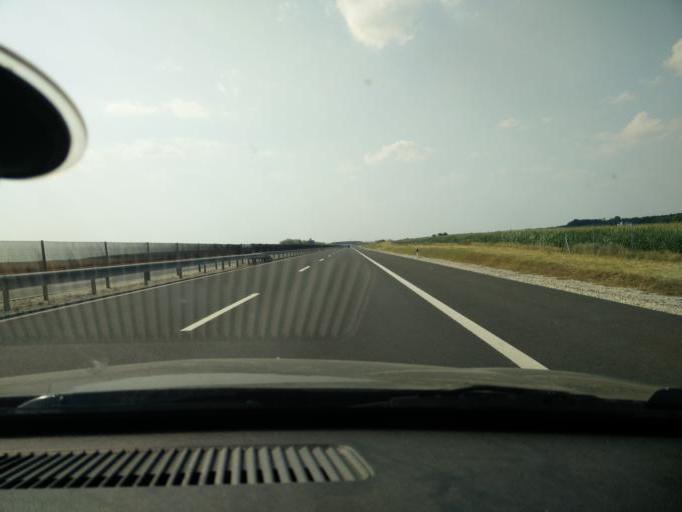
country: HU
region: Tolna
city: Tolna
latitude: 46.4235
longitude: 18.7250
